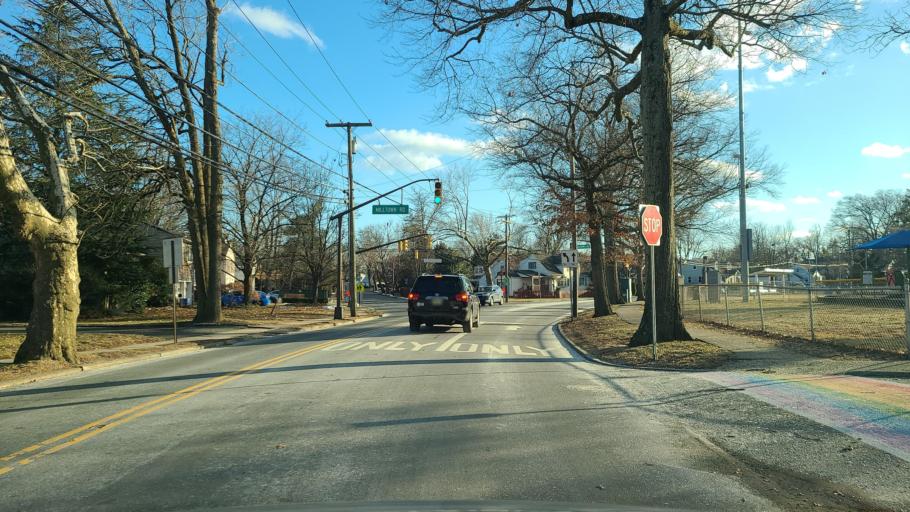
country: US
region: New Jersey
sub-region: Union County
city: Springfield
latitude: 40.7000
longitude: -74.3178
